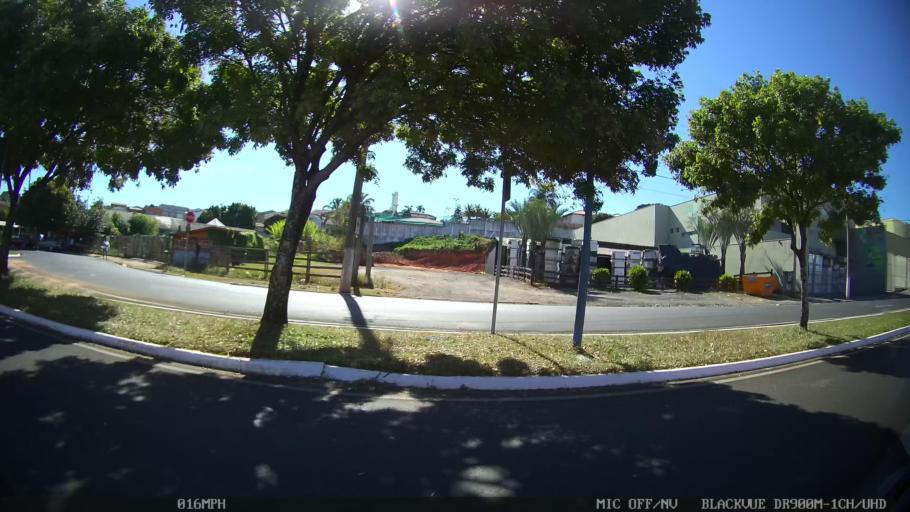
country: BR
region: Sao Paulo
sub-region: Franca
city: Franca
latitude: -20.5219
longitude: -47.3734
